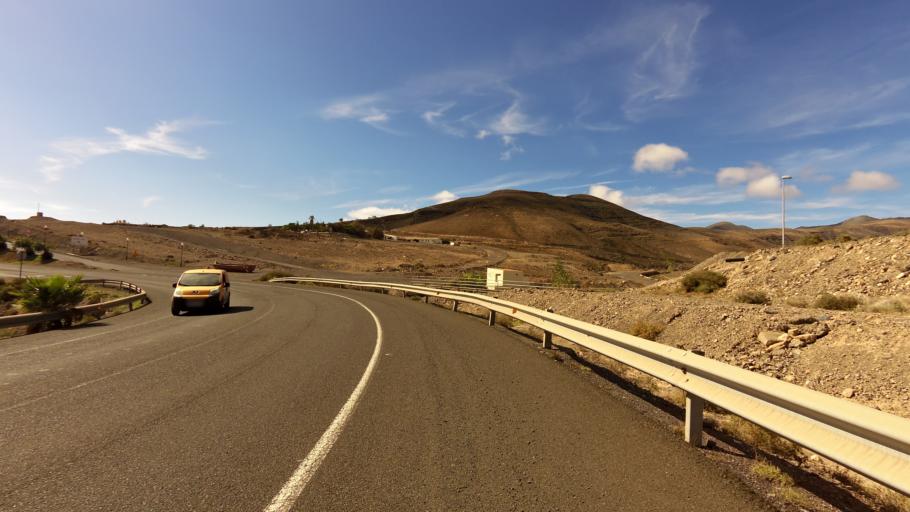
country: ES
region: Canary Islands
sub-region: Provincia de Las Palmas
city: Pajara
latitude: 28.0605
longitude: -14.3194
